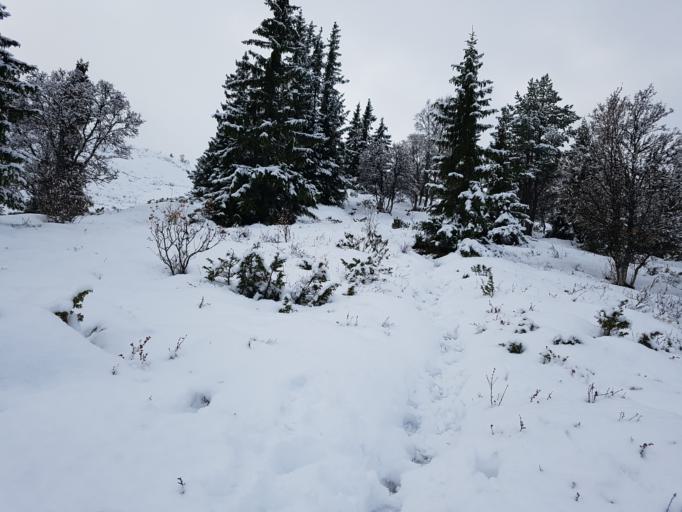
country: NO
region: Oppland
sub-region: Sel
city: Otta
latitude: 61.8058
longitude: 9.6778
